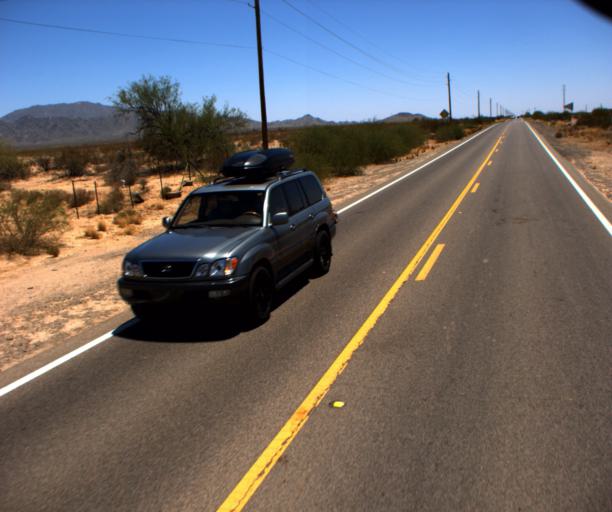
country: US
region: Arizona
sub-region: Pinal County
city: Maricopa
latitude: 33.0620
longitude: -112.2457
